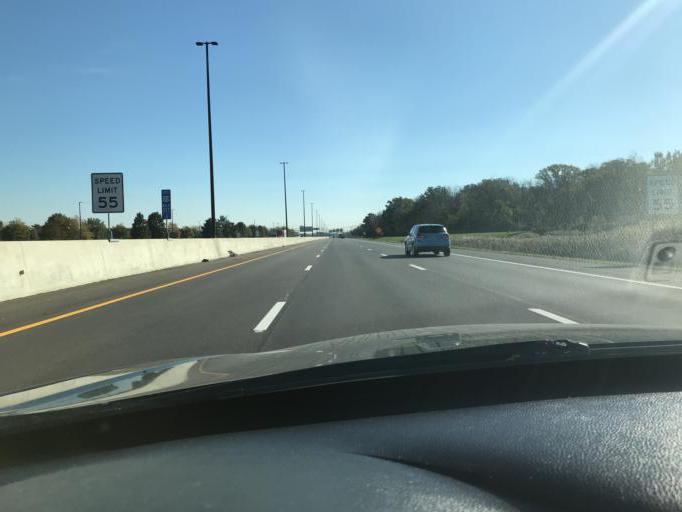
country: US
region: Ohio
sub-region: Franklin County
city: Dublin
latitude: 40.0989
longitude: -83.1579
